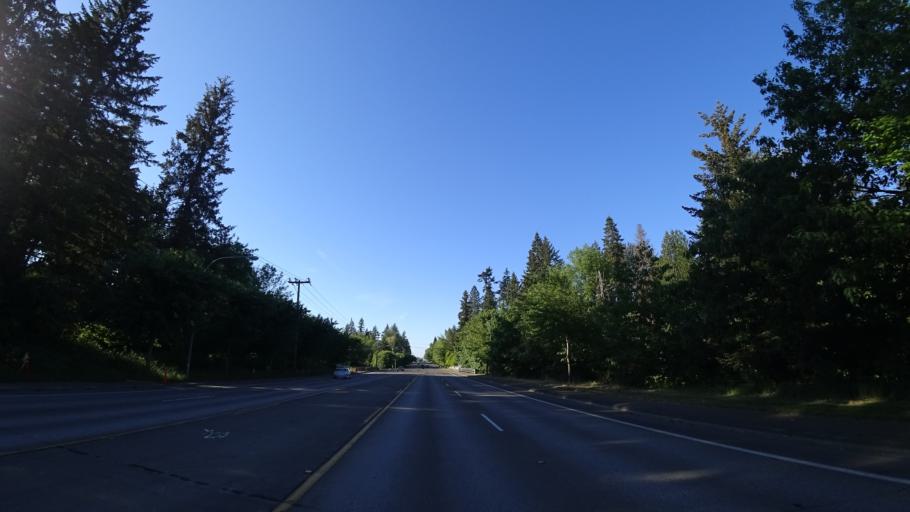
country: US
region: Oregon
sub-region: Washington County
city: Aloha
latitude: 45.5059
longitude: -122.8674
